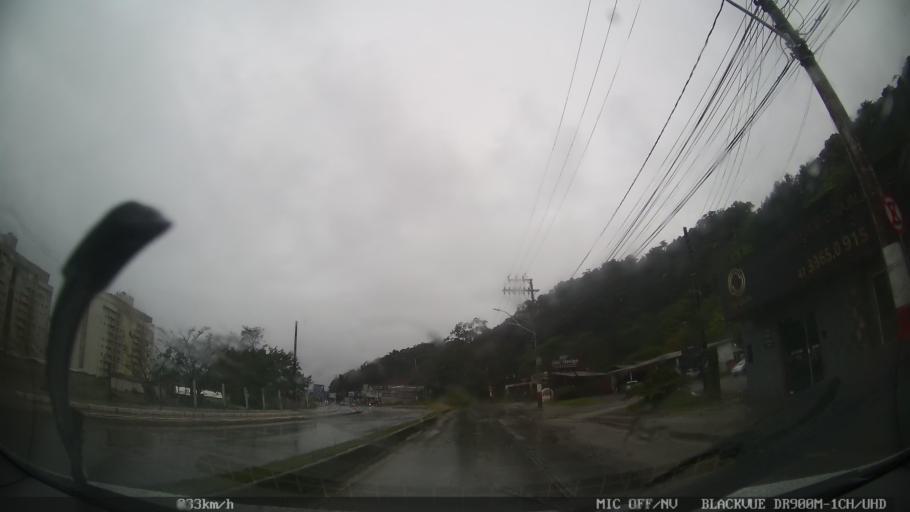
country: BR
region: Santa Catarina
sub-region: Balneario Camboriu
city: Balneario Camboriu
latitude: -27.0092
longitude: -48.6490
